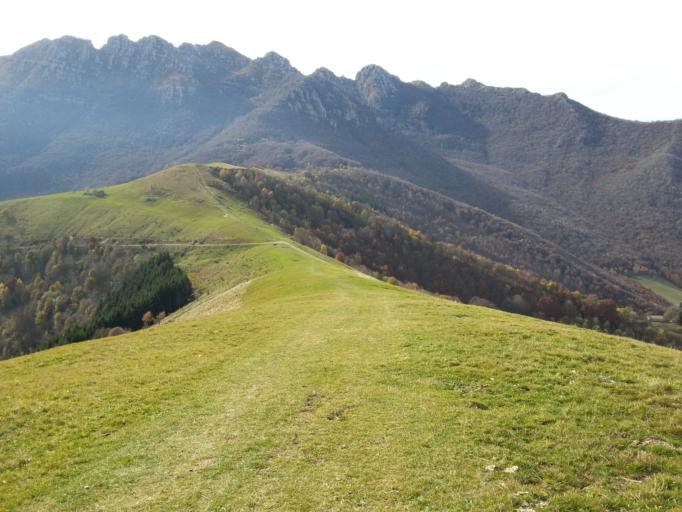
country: IT
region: Lombardy
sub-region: Provincia di Bergamo
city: Brumano
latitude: 45.8679
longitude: 9.4975
